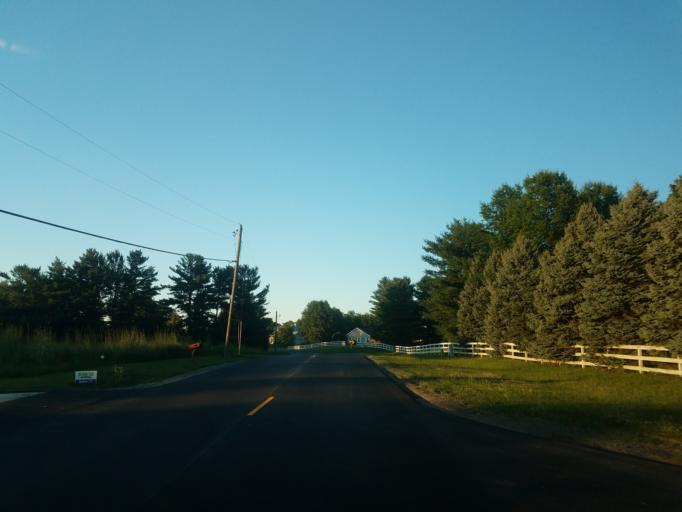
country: US
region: Illinois
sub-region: McLean County
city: Bloomington
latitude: 40.4558
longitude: -89.0360
